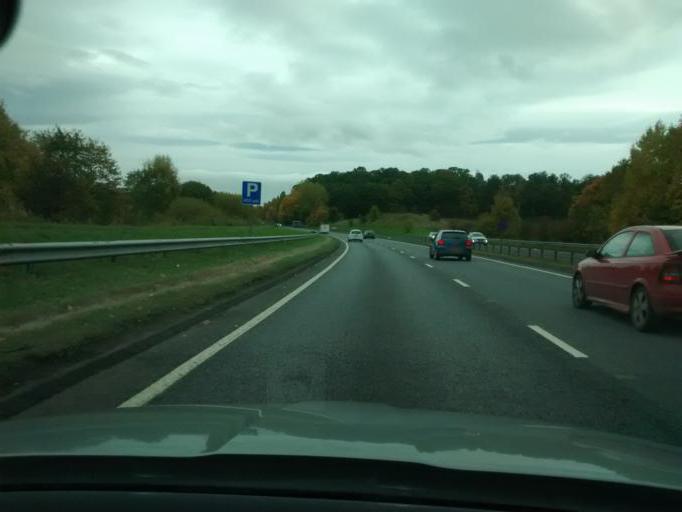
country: GB
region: Scotland
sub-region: Perth and Kinross
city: Luncarty
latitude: 56.4341
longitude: -3.4731
